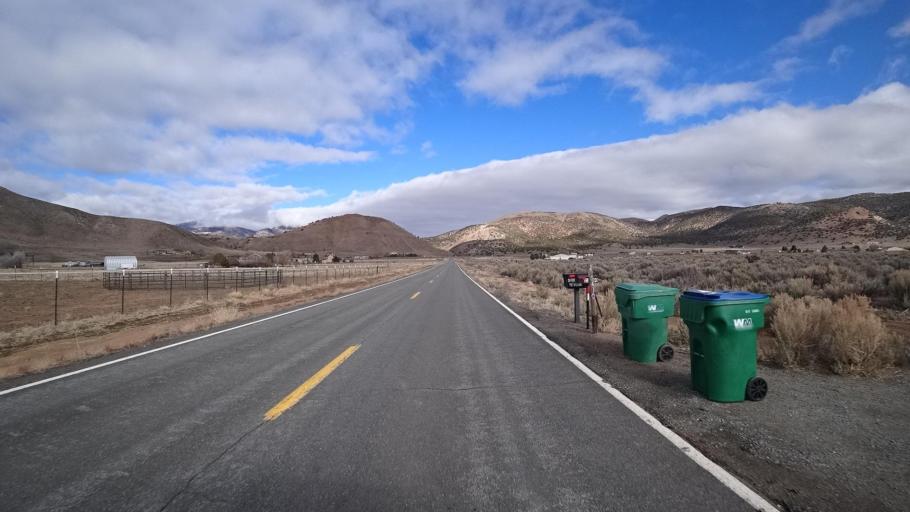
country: US
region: Nevada
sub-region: Washoe County
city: Cold Springs
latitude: 39.8927
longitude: -119.9779
